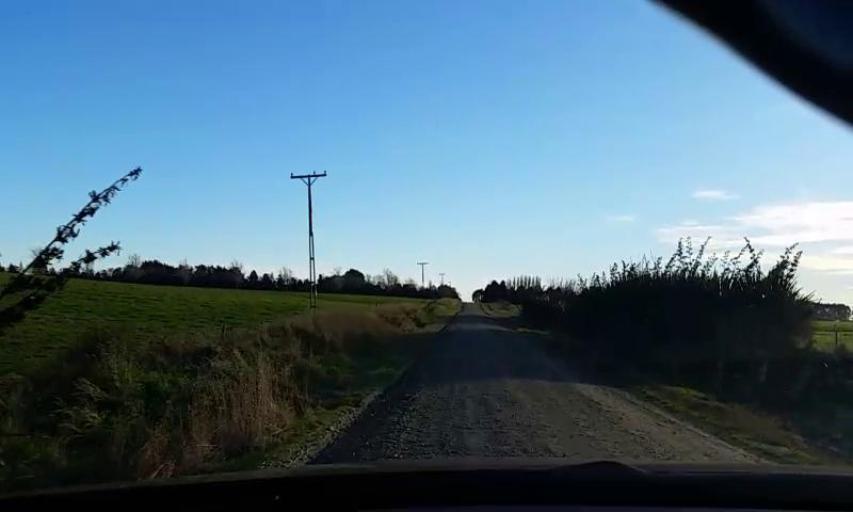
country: NZ
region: Southland
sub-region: Invercargill City
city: Invercargill
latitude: -46.2850
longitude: 168.5040
